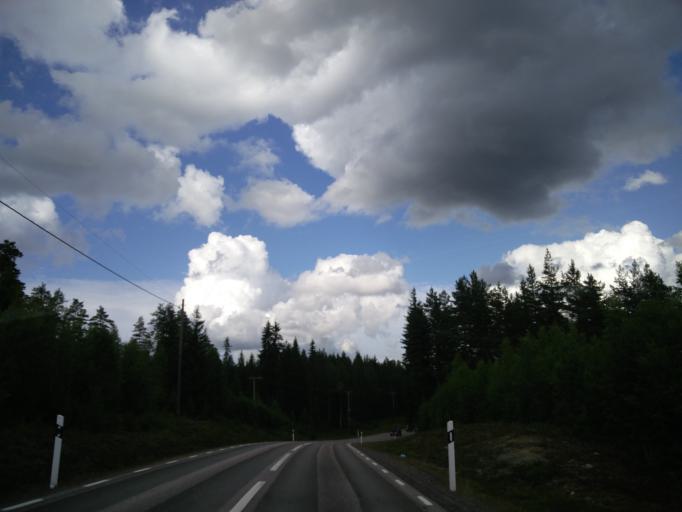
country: SE
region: Vaermland
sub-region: Torsby Kommun
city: Torsby
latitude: 60.3132
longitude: 13.0987
